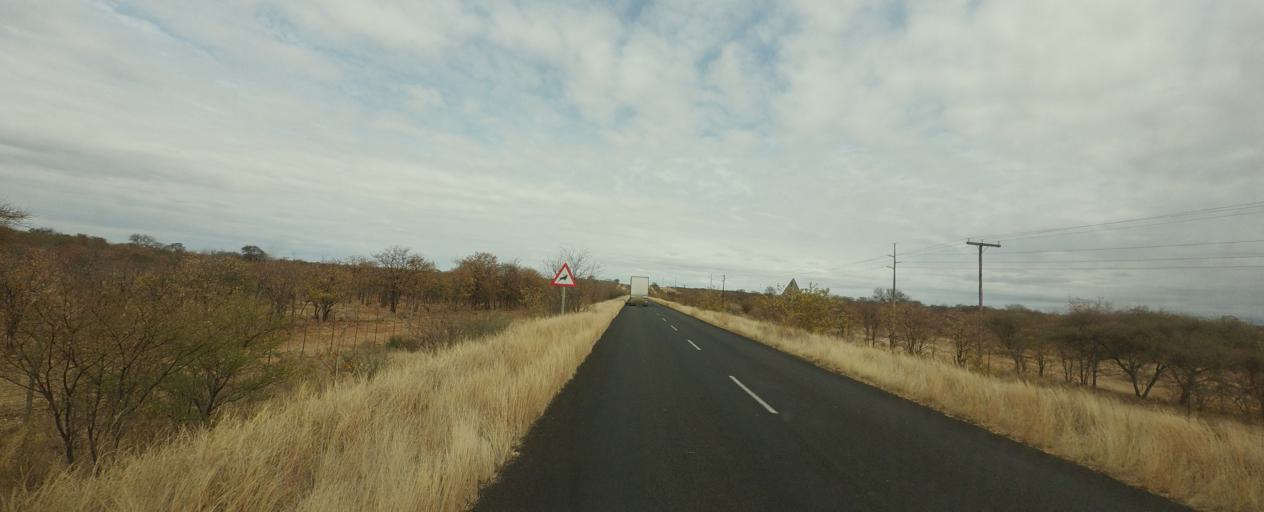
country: ZW
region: Matabeleland South
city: Beitbridge
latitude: -22.4300
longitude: 29.4336
